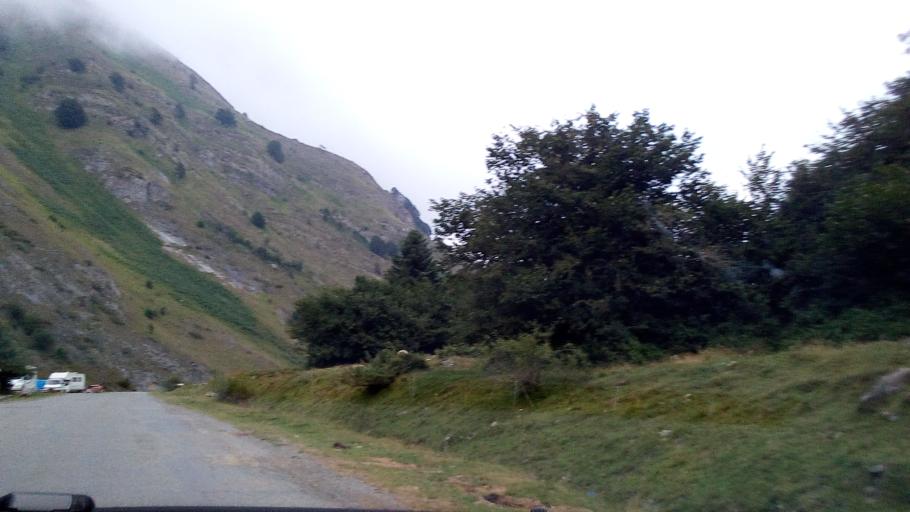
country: FR
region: Midi-Pyrenees
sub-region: Departement des Hautes-Pyrenees
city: Cauterets
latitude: 42.9072
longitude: -0.2042
